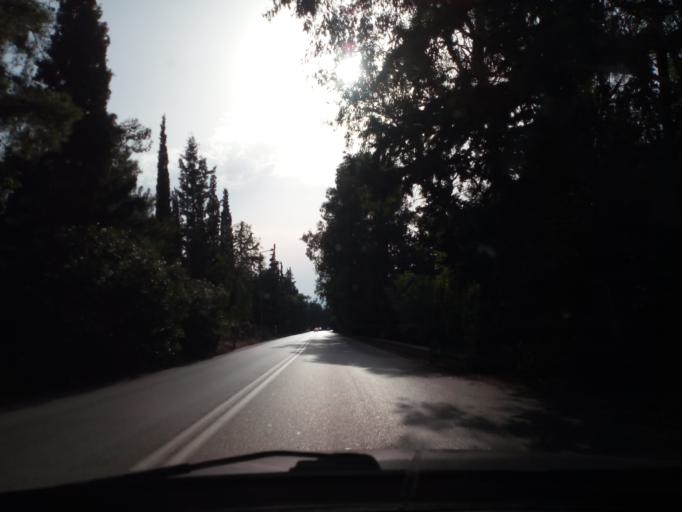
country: GR
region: Attica
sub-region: Nomos Attikis
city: Zografos
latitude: 37.9658
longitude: 23.7863
